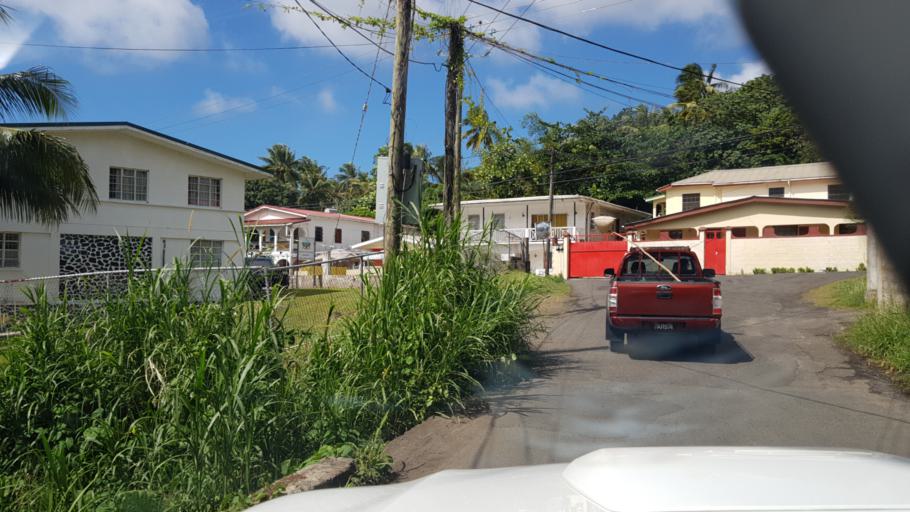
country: LC
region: Castries Quarter
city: Bisee
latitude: 14.0151
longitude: -60.9567
